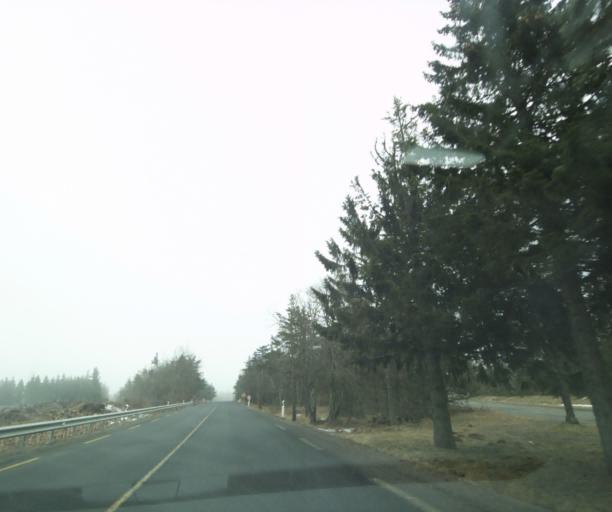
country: FR
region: Languedoc-Roussillon
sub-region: Departement de la Lozere
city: Langogne
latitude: 44.7570
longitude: 3.9278
